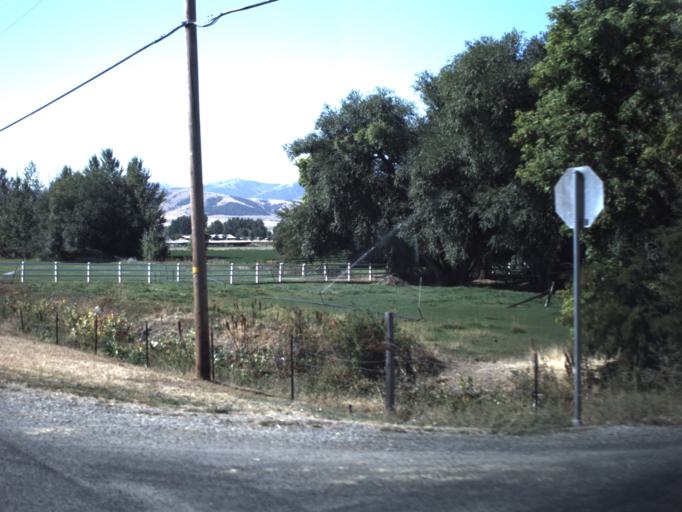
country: US
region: Utah
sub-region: Cache County
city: Hyrum
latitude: 41.5908
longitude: -111.8372
